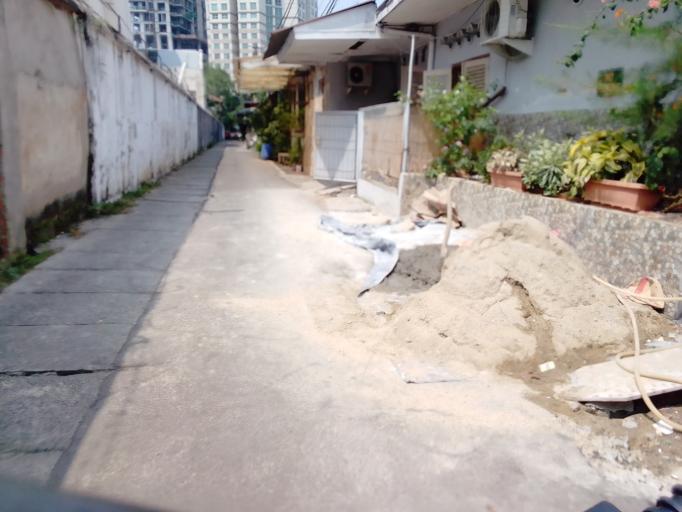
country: ID
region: Jakarta Raya
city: Jakarta
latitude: -6.2114
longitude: 106.8112
